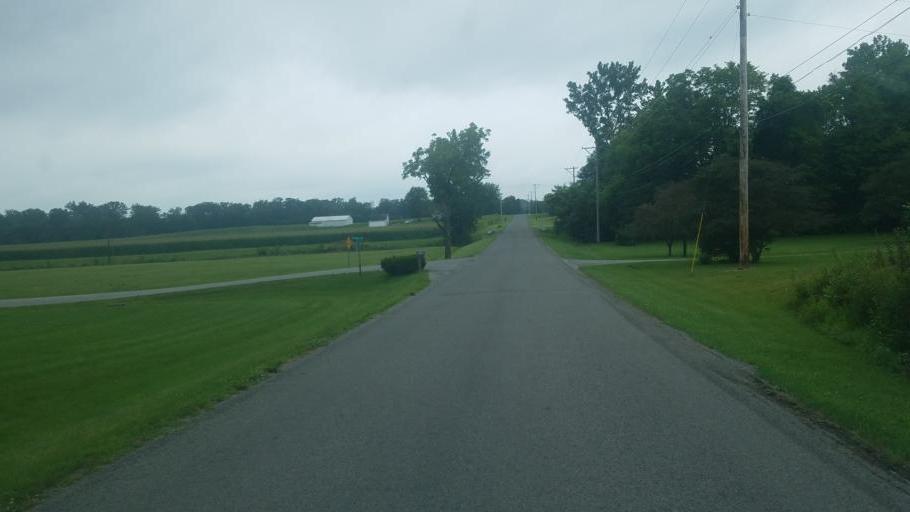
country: US
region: Ohio
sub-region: Logan County
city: Russells Point
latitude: 40.4629
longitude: -83.8574
